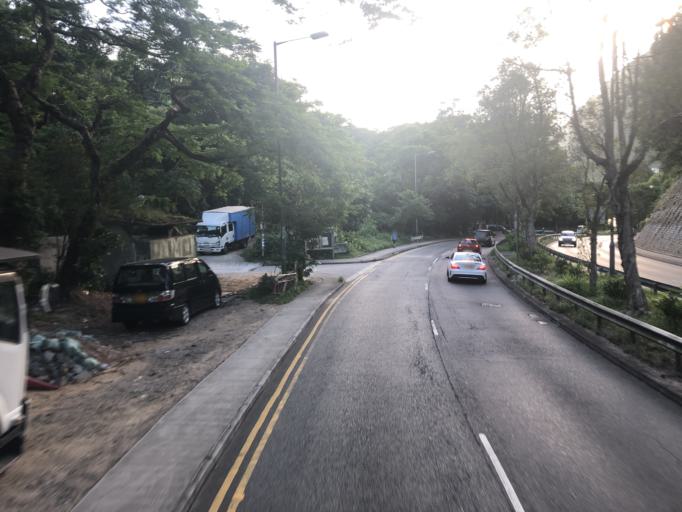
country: HK
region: Kowloon City
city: Kowloon
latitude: 22.3332
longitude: 114.2345
